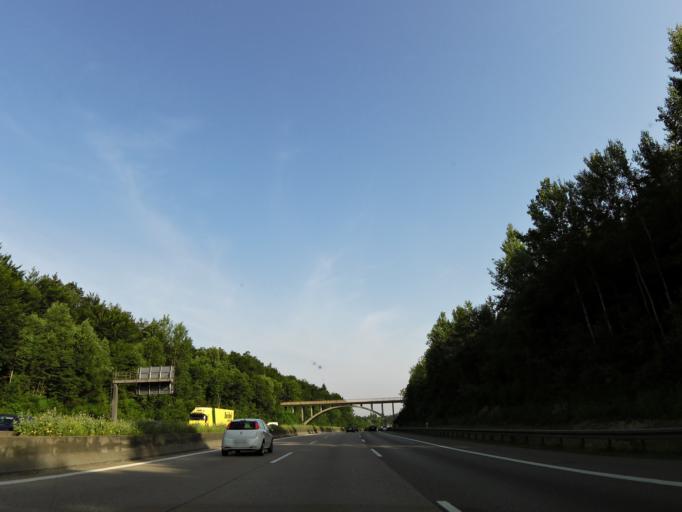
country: DE
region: Baden-Wuerttemberg
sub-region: Regierungsbezirk Stuttgart
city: Sindelfingen
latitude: 48.7366
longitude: 9.0400
